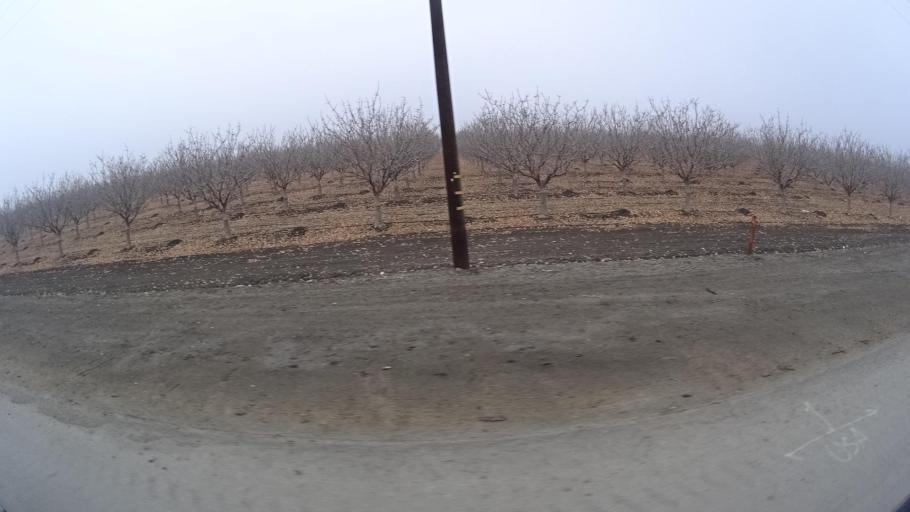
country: US
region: California
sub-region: Kern County
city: Buttonwillow
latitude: 35.4050
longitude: -119.5185
